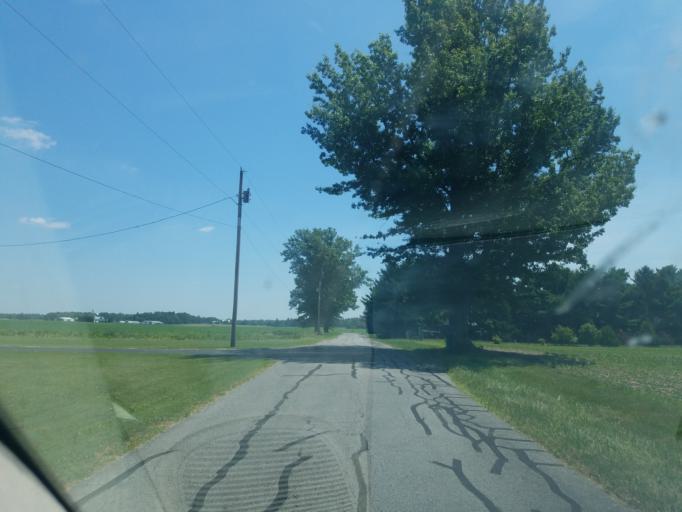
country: US
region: Ohio
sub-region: Hancock County
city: Arlington
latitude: 40.8632
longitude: -83.7100
